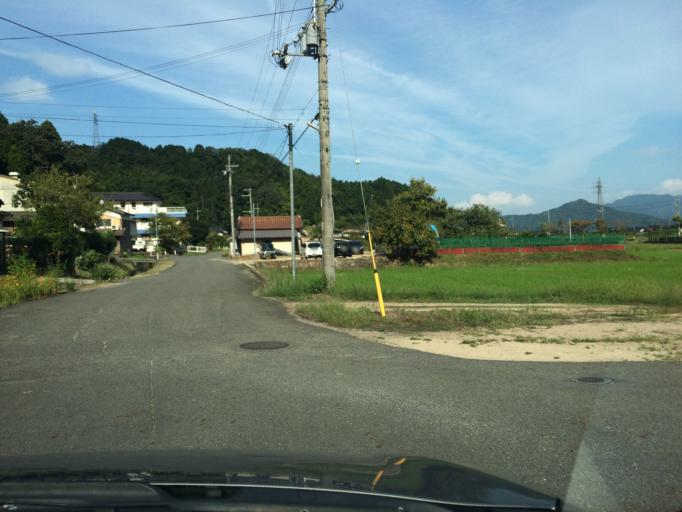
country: JP
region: Hyogo
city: Toyooka
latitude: 35.5102
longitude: 134.8117
